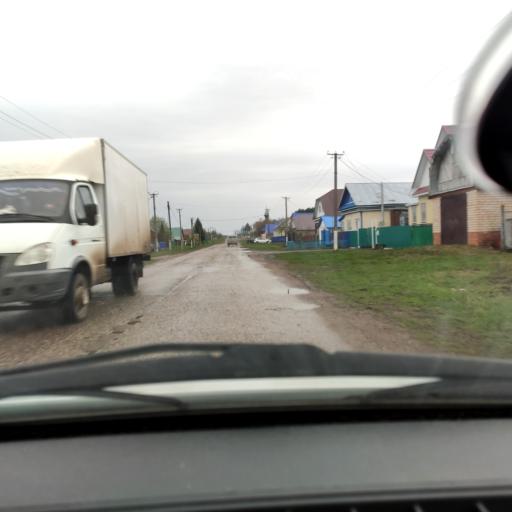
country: RU
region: Bashkortostan
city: Tolbazy
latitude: 54.1717
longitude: 55.9549
